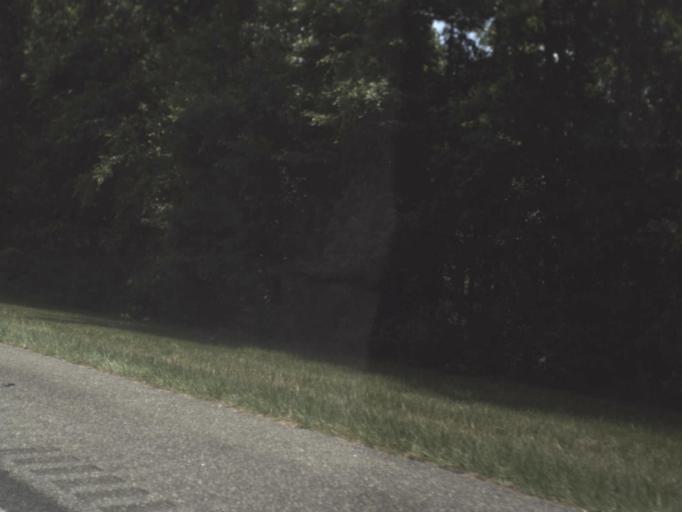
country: US
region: Florida
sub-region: Madison County
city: Madison
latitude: 30.4301
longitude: -83.5592
